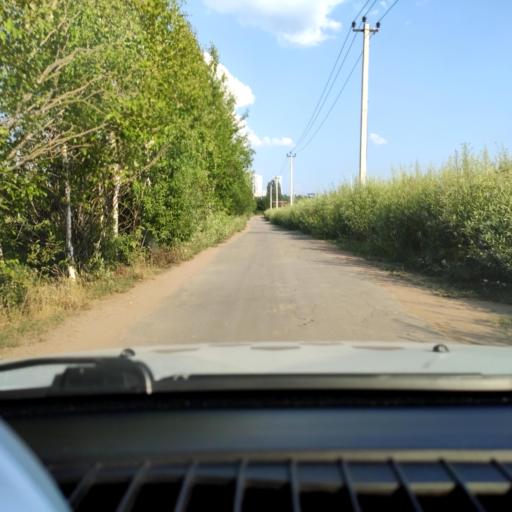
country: RU
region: Perm
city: Perm
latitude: 58.0294
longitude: 56.2359
